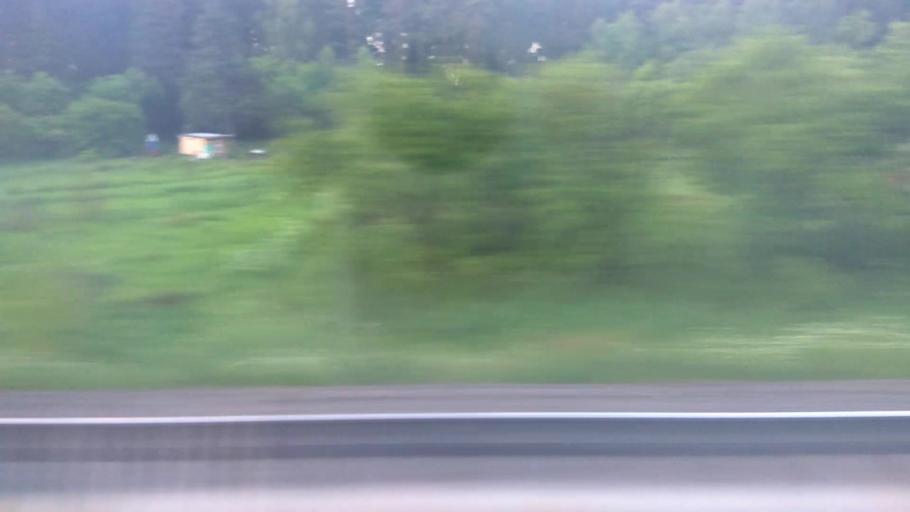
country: RU
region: Moskovskaya
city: Belyye Stolby
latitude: 55.3626
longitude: 37.8294
